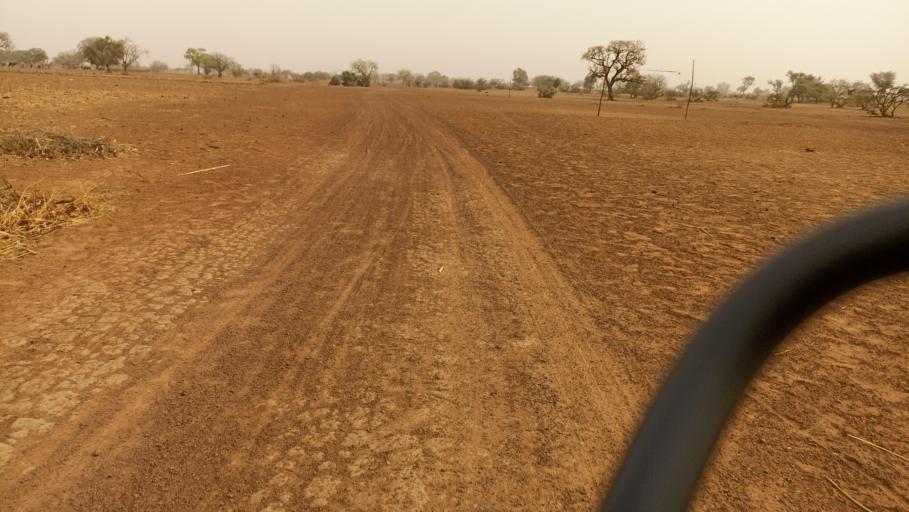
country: BF
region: Nord
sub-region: Province du Zondoma
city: Gourcy
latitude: 13.1428
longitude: -2.5972
